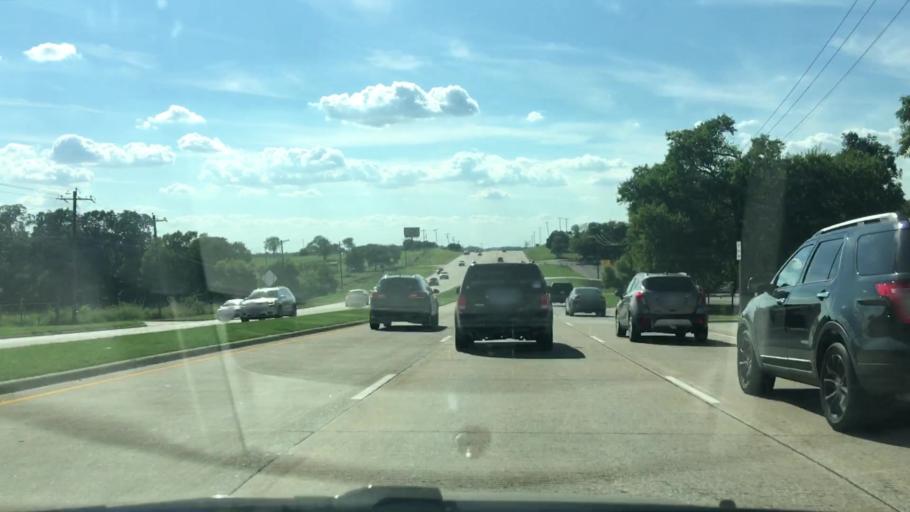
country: US
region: Texas
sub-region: Collin County
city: McKinney
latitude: 33.2179
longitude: -96.6692
